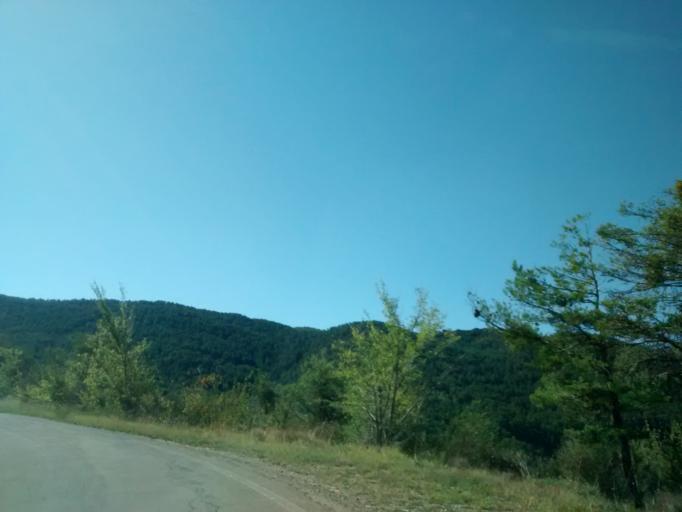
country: ES
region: Aragon
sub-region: Provincia de Huesca
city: Jaca
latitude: 42.5107
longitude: -0.5588
